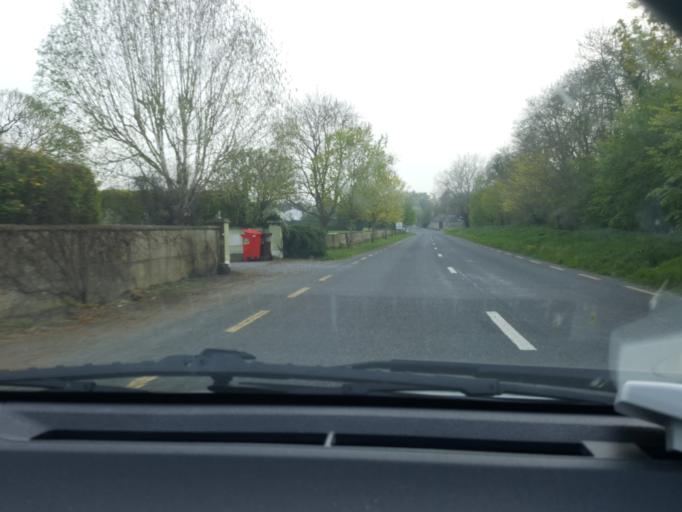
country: IE
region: Munster
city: Cahir
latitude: 52.3865
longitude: -7.9125
